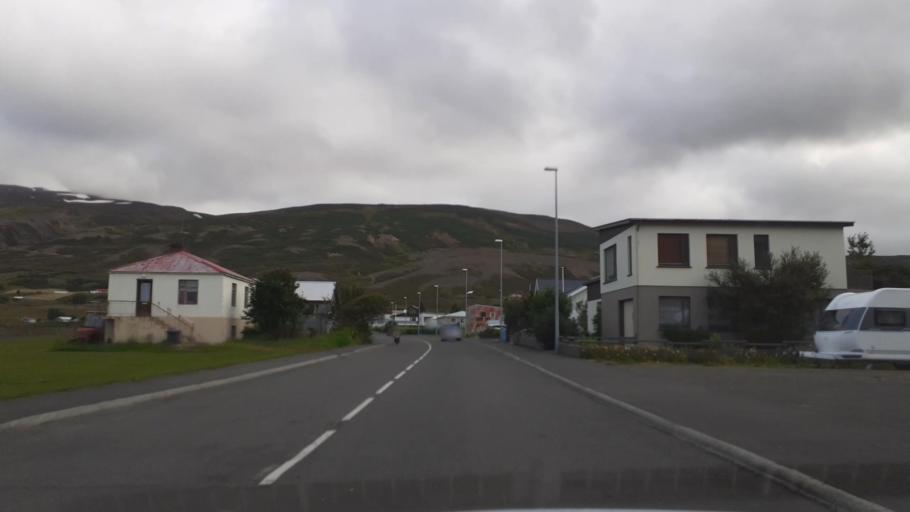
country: IS
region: Northeast
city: Akureyri
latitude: 65.9476
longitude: -18.1836
